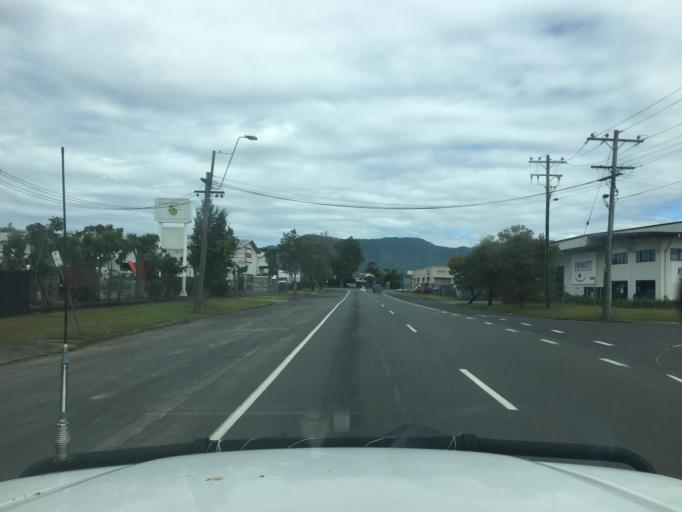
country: AU
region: Queensland
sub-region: Cairns
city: Cairns
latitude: -16.9362
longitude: 145.7691
